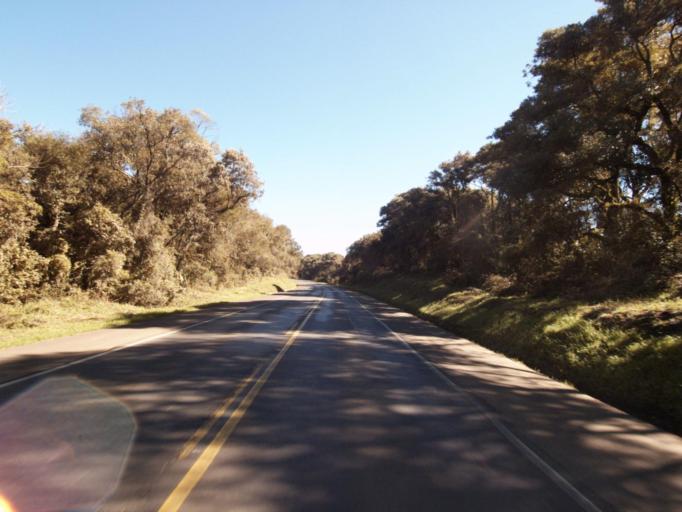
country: BR
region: Santa Catarina
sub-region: Xanxere
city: Xanxere
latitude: -26.8826
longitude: -52.1667
